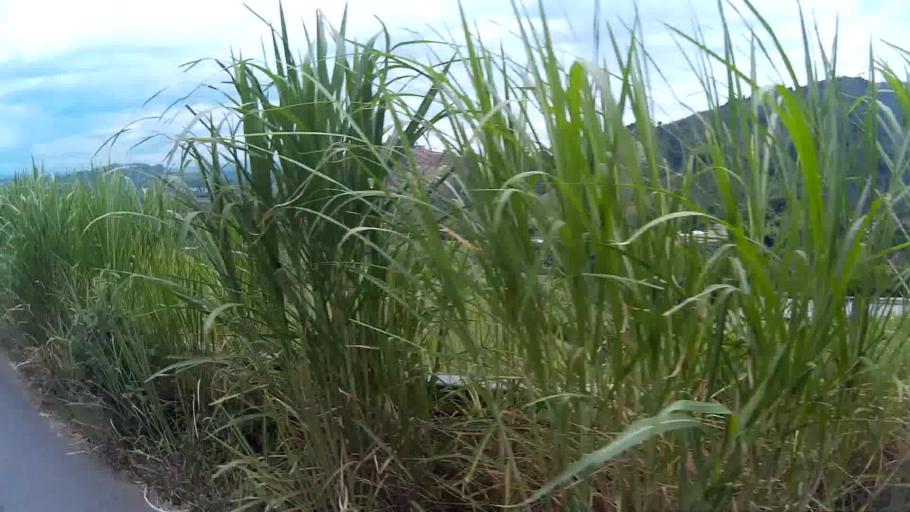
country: CO
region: Risaralda
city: Marsella
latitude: 4.8646
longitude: -75.7603
